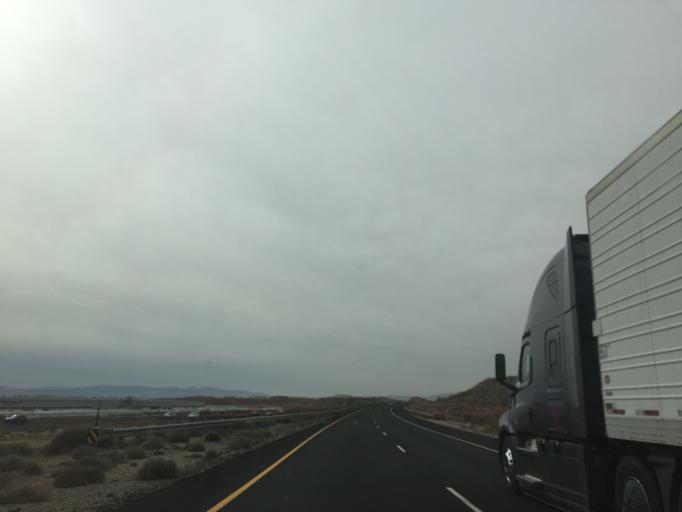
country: US
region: Utah
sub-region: Washington County
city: Washington
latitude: 37.1793
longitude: -113.4201
